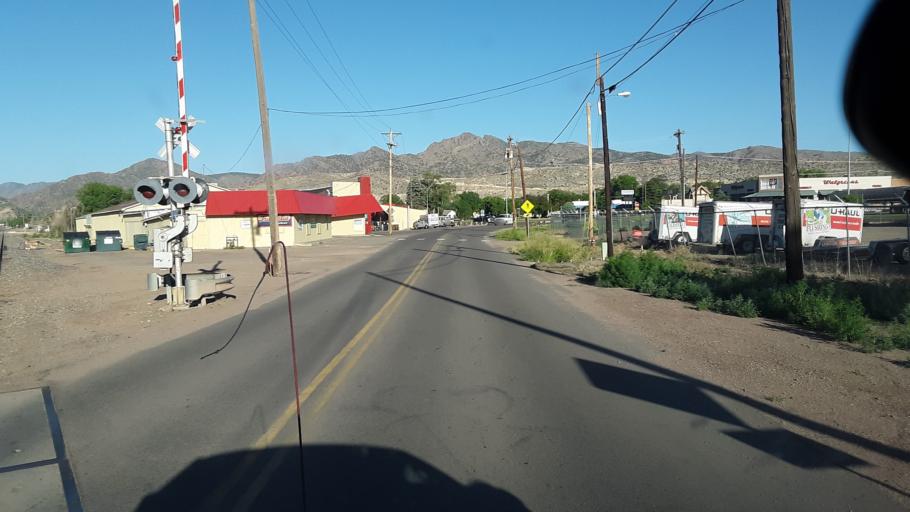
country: US
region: Colorado
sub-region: Fremont County
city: Lincoln Park
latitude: 38.4467
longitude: -105.2232
